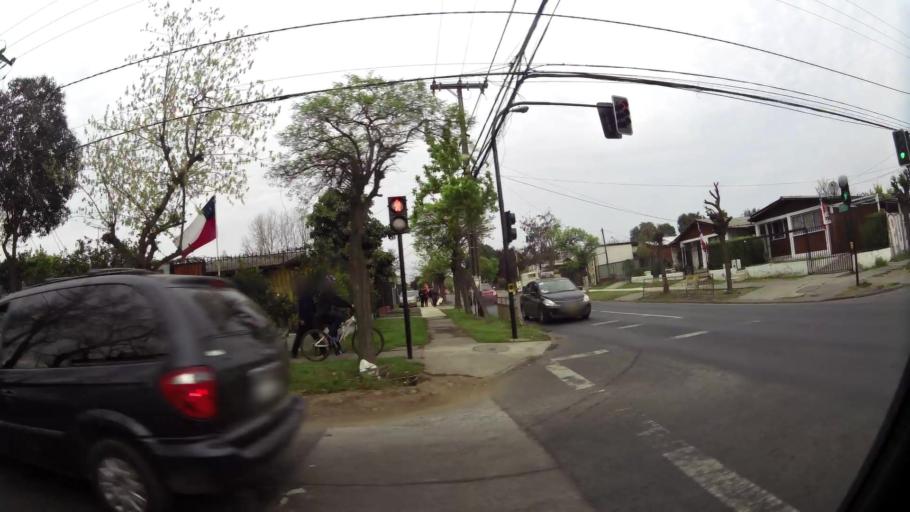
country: CL
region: Santiago Metropolitan
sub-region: Provincia de Santiago
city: Lo Prado
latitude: -33.5178
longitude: -70.7688
